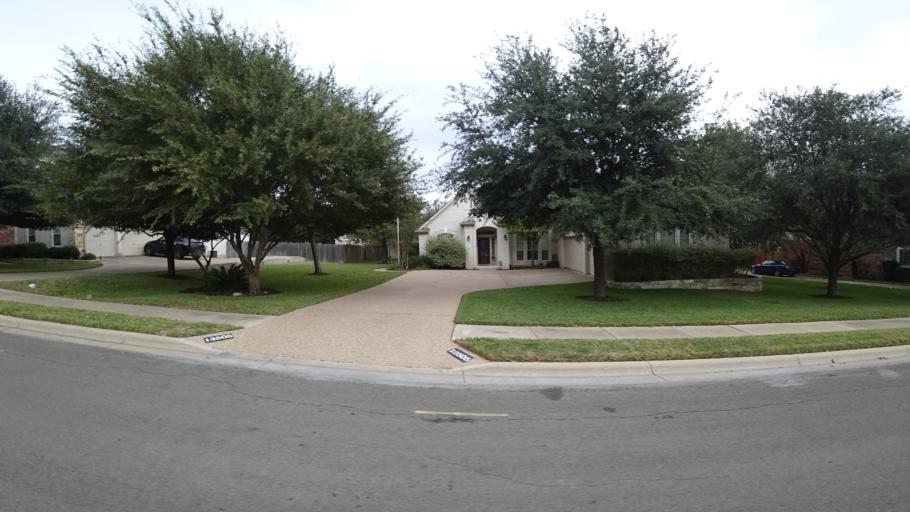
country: US
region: Texas
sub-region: Travis County
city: Shady Hollow
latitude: 30.1489
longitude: -97.8584
